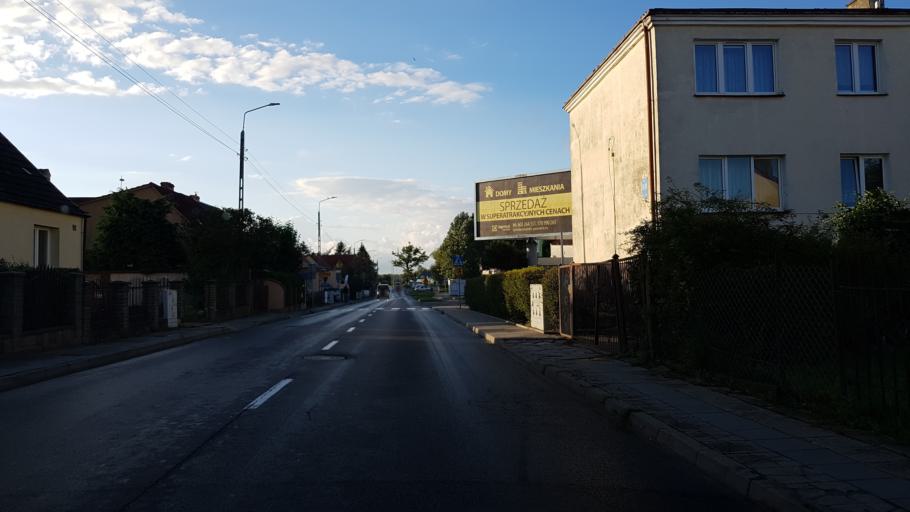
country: PL
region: West Pomeranian Voivodeship
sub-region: Koszalin
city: Koszalin
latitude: 54.2057
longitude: 16.1631
